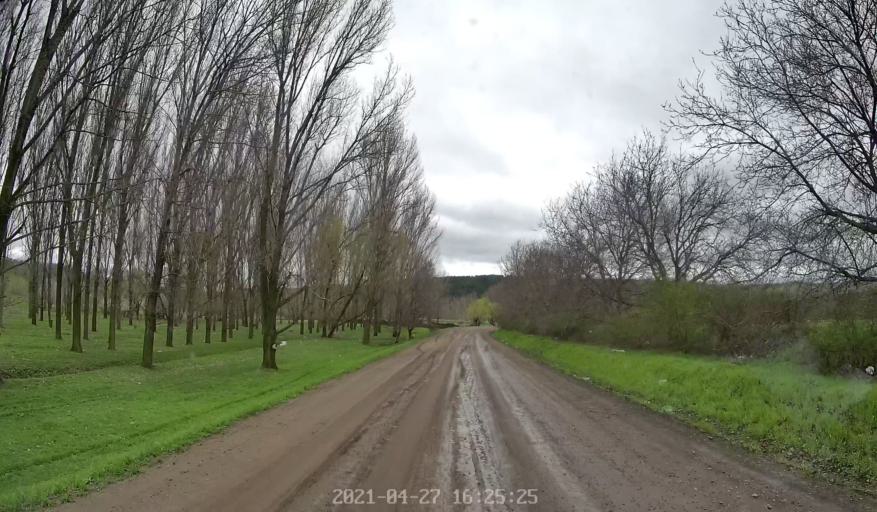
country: MD
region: Chisinau
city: Singera
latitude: 46.9852
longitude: 29.0221
